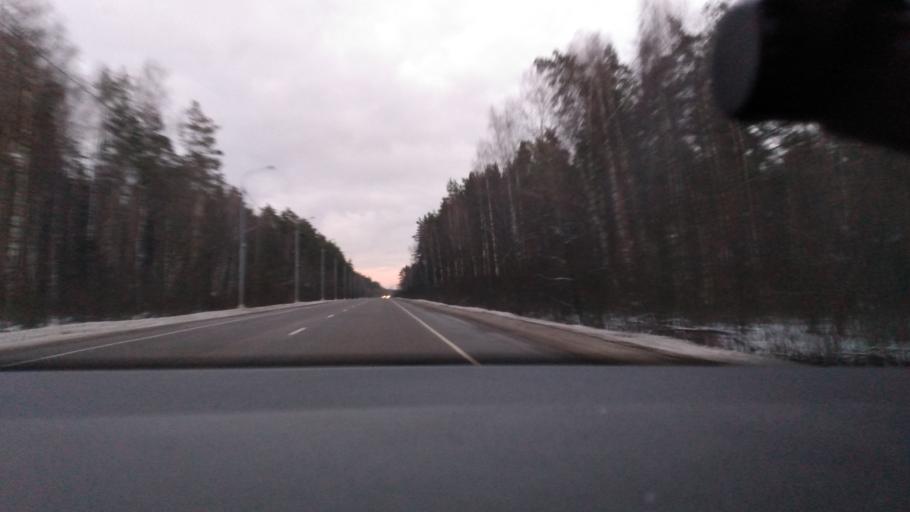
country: RU
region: Moskovskaya
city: Yegor'yevsk
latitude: 55.4530
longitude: 38.9993
